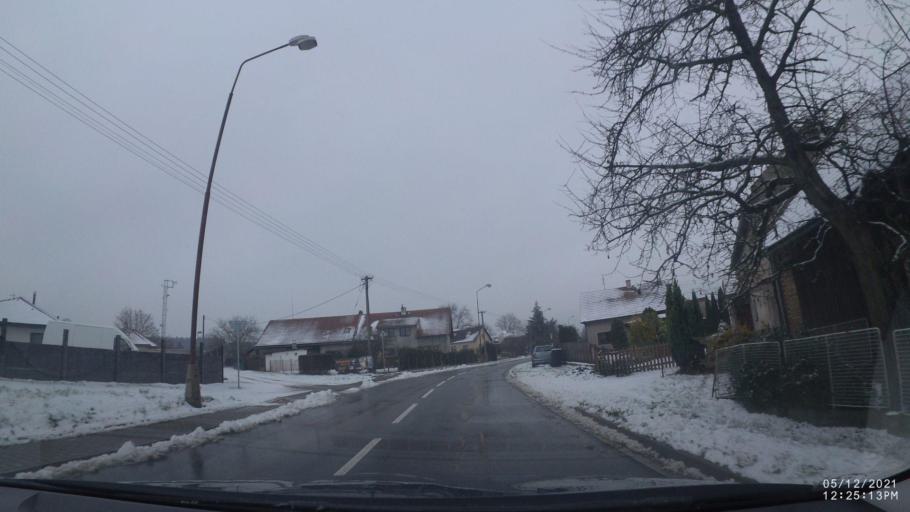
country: CZ
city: Ceske Mezirici
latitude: 50.3214
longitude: 16.0870
